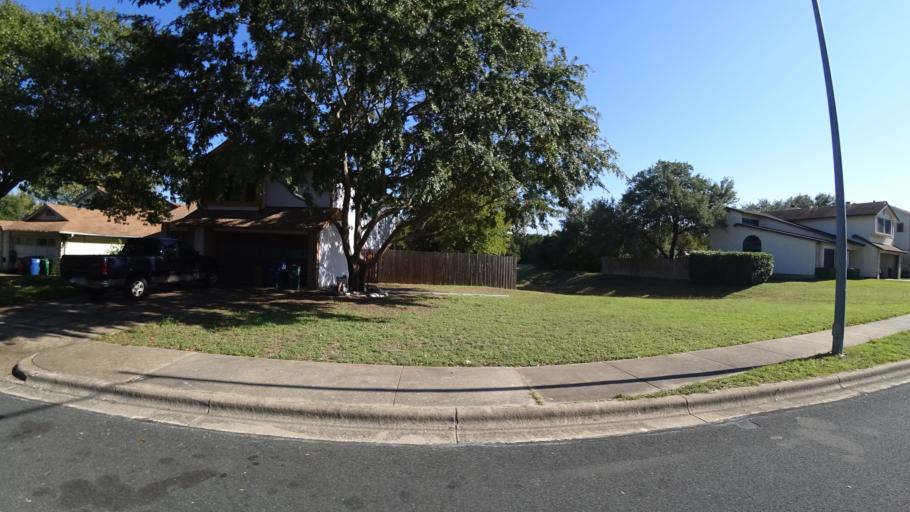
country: US
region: Texas
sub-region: Travis County
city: Shady Hollow
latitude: 30.2008
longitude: -97.8464
